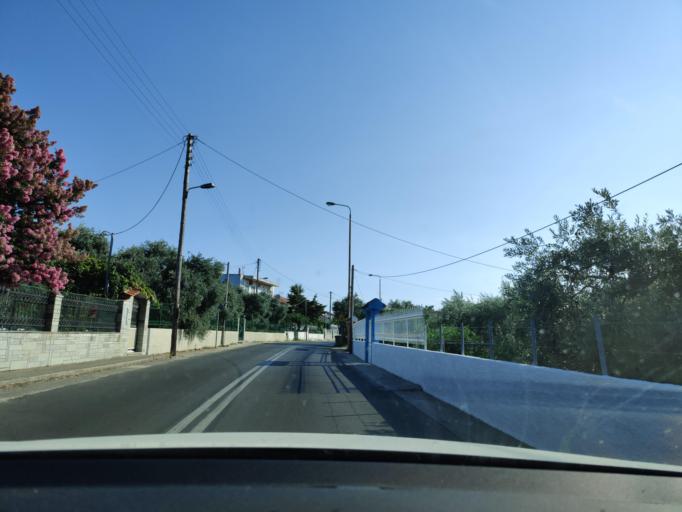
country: GR
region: East Macedonia and Thrace
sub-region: Nomos Kavalas
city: Prinos
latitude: 40.7036
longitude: 24.5308
